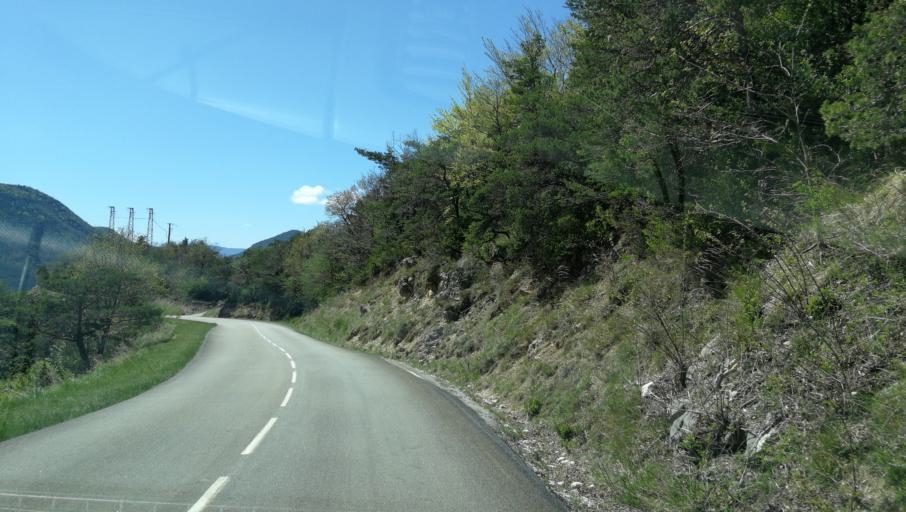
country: FR
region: Rhone-Alpes
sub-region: Departement de la Drome
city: Die
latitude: 44.8232
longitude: 5.3952
